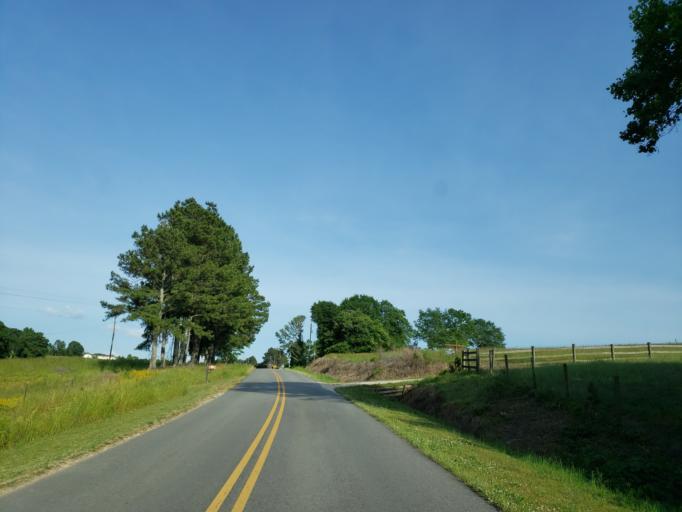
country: US
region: Georgia
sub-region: Carroll County
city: Bowdon
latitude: 33.5013
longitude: -85.3260
